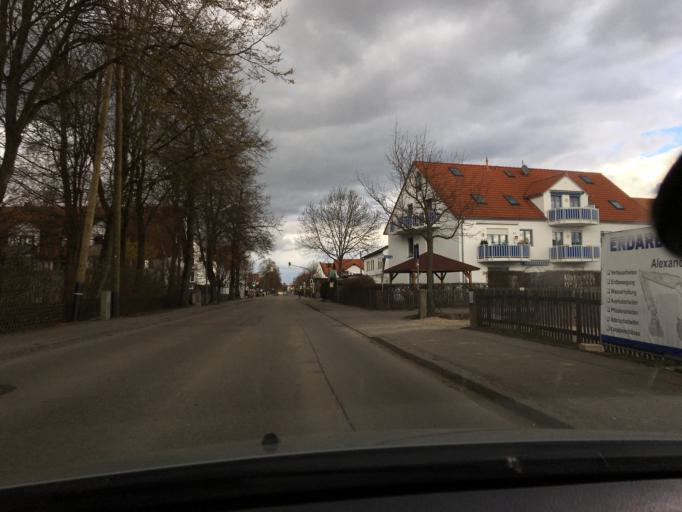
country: DE
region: Bavaria
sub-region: Upper Bavaria
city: Hallbergmoos
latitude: 48.3106
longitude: 11.7420
